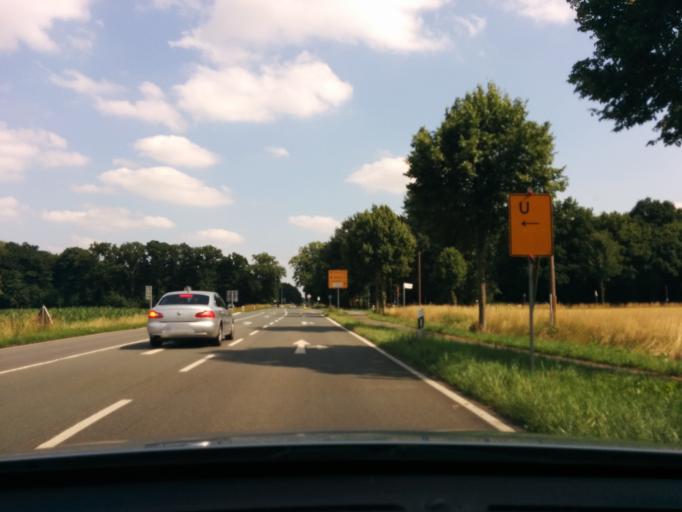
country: DE
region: North Rhine-Westphalia
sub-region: Regierungsbezirk Munster
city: Metelen
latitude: 52.1922
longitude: 7.2512
